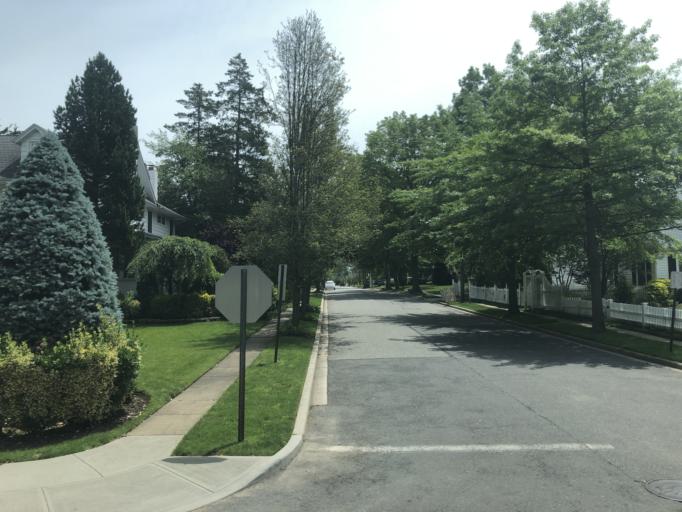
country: US
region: New York
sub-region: Nassau County
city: Rockville Centre
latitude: 40.6662
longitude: -73.6420
